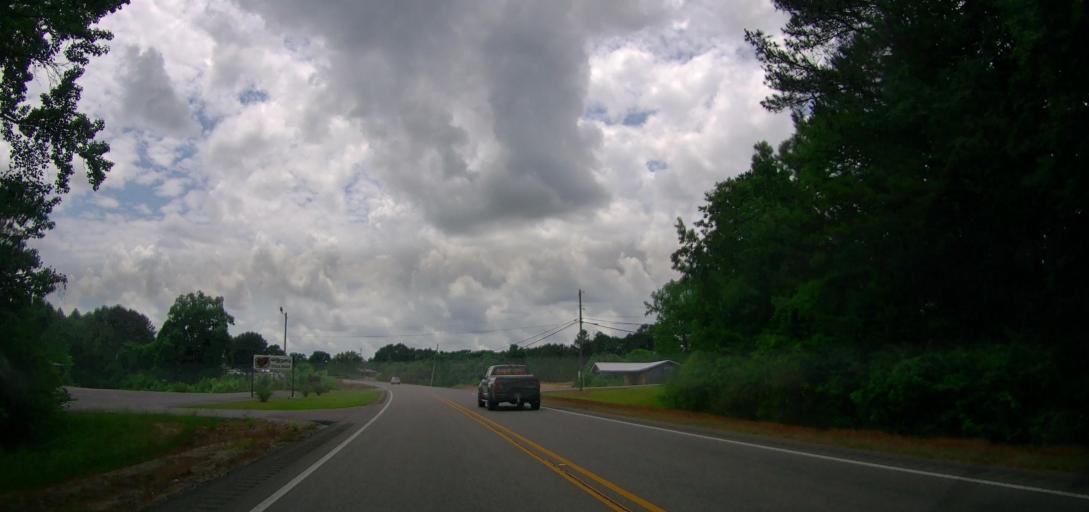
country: US
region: Alabama
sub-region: Marion County
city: Hamilton
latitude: 34.1371
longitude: -88.0152
